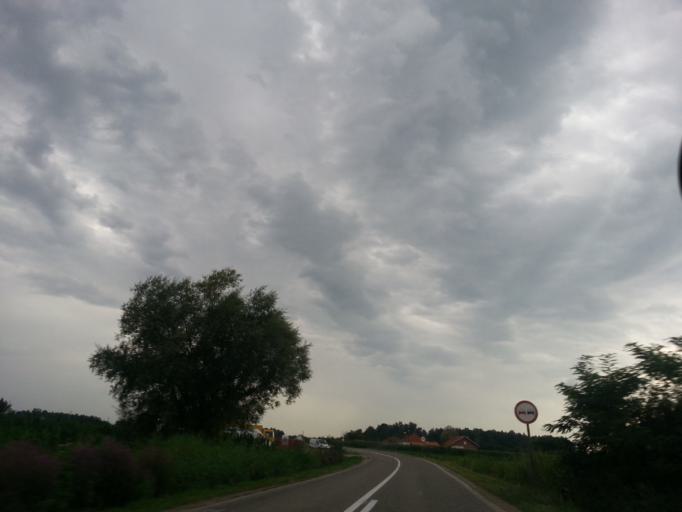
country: BA
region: Republika Srpska
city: Velika Obarska
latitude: 44.7697
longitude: 19.1457
